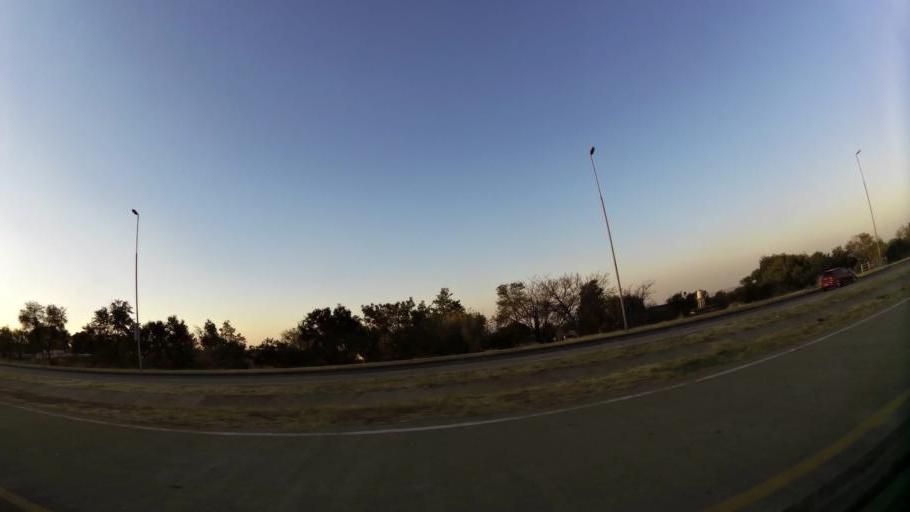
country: ZA
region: North-West
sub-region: Bojanala Platinum District Municipality
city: Rustenburg
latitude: -25.6420
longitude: 27.2035
